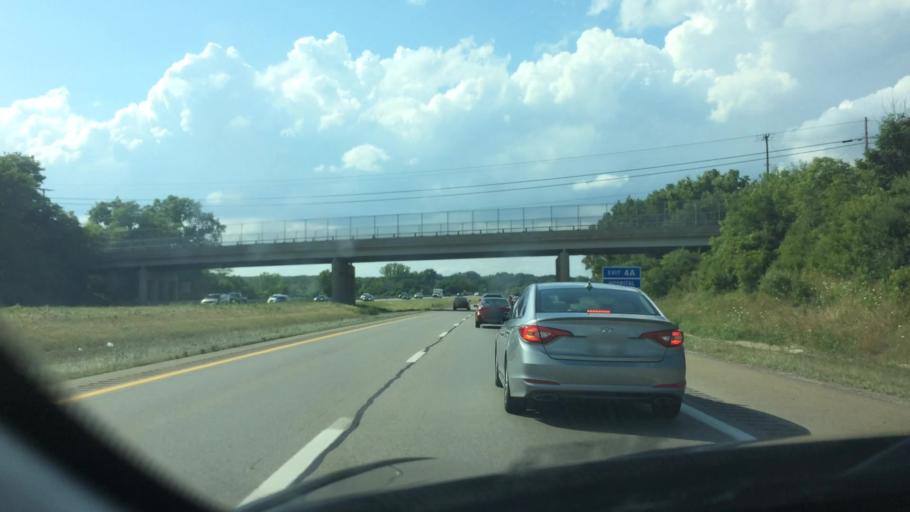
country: US
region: Ohio
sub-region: Lucas County
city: Maumee
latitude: 41.5404
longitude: -83.6786
